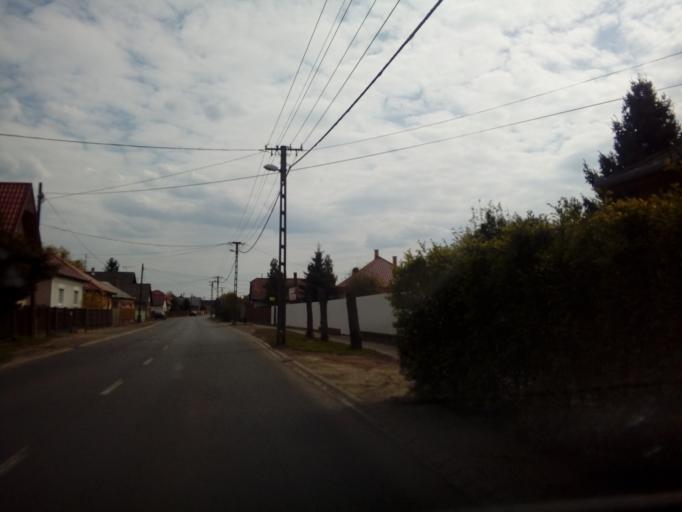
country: HU
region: Szabolcs-Szatmar-Bereg
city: Nagykallo
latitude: 47.8684
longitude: 21.8480
